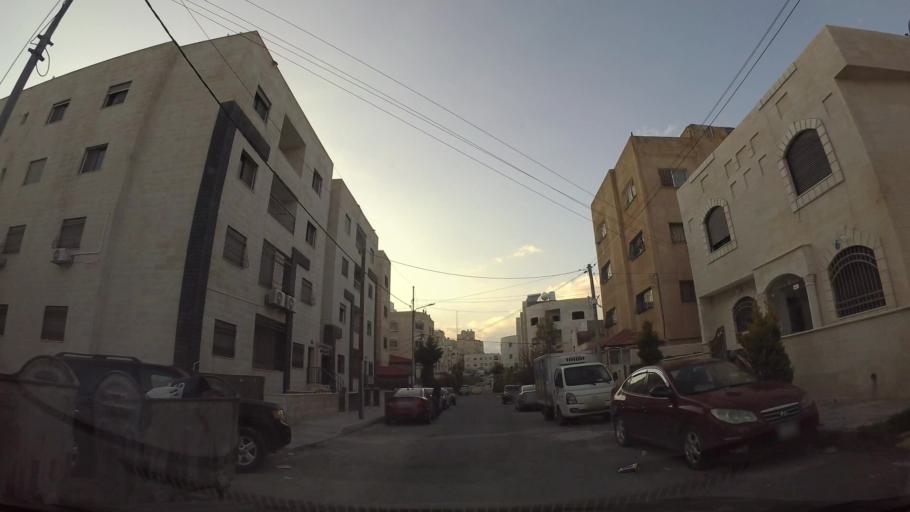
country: JO
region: Amman
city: Al Bunayyat ash Shamaliyah
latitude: 31.9138
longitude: 35.8910
